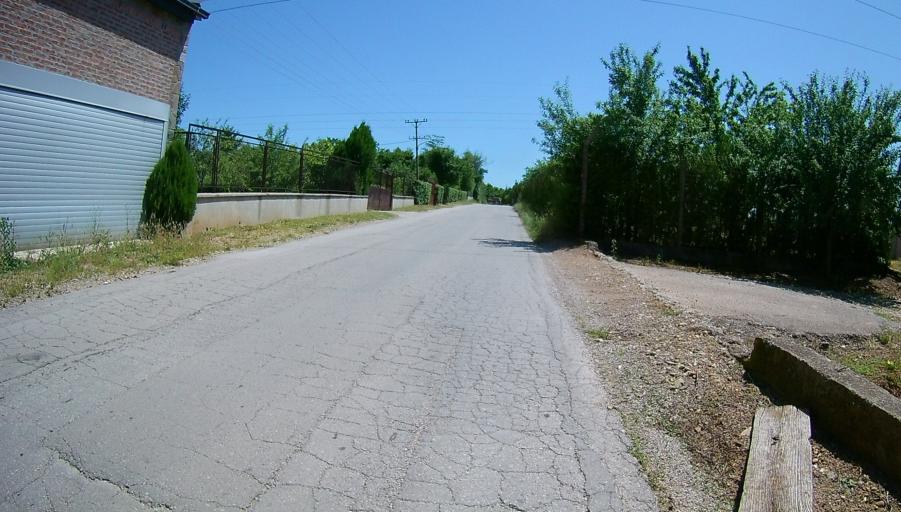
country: RS
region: Central Serbia
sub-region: Nisavski Okrug
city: Nis
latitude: 43.2915
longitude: 21.9008
